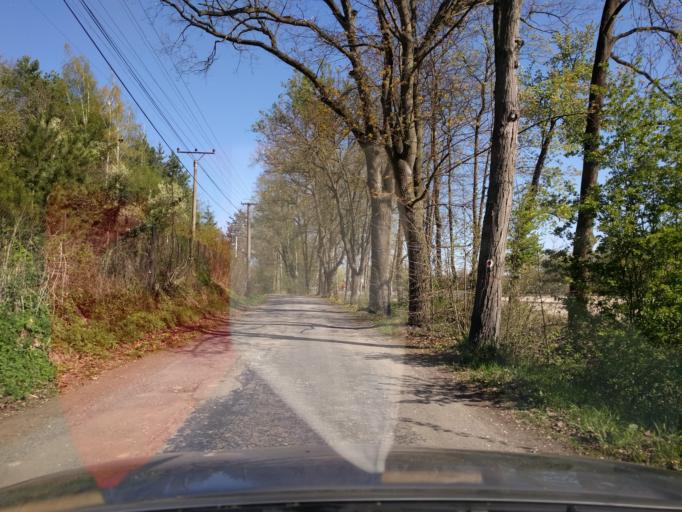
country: CZ
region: Central Bohemia
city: Cesky Brod
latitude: 50.0468
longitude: 14.8419
